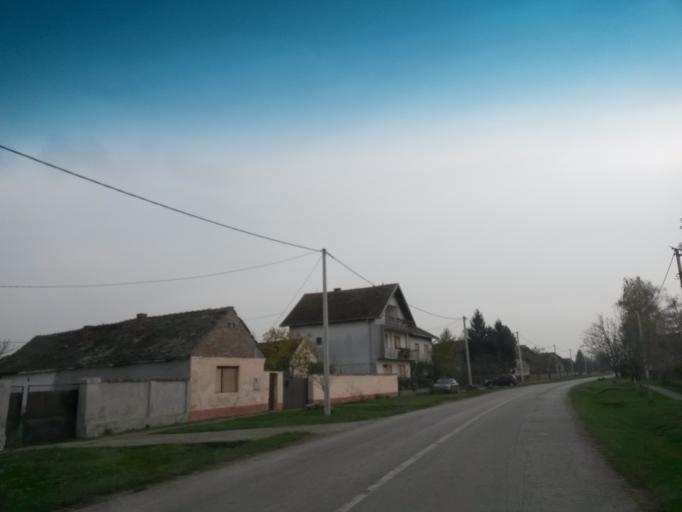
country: HR
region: Vukovarsko-Srijemska
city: Nustar
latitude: 45.3692
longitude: 18.8539
